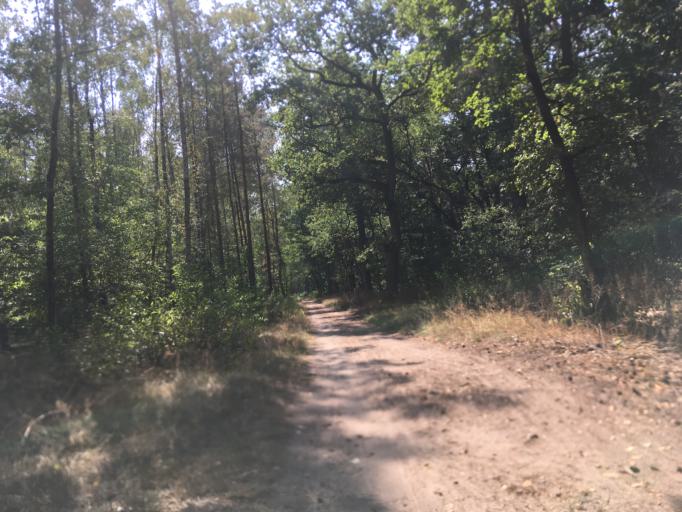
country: DE
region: Berlin
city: Friedrichshagen
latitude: 52.4680
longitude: 13.6061
